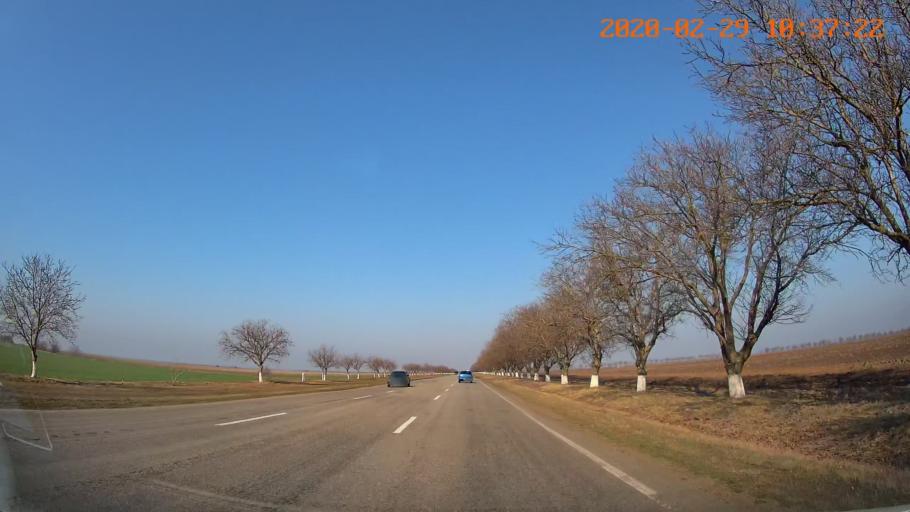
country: MD
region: Anenii Noi
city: Varnita
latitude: 47.0051
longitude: 29.4909
